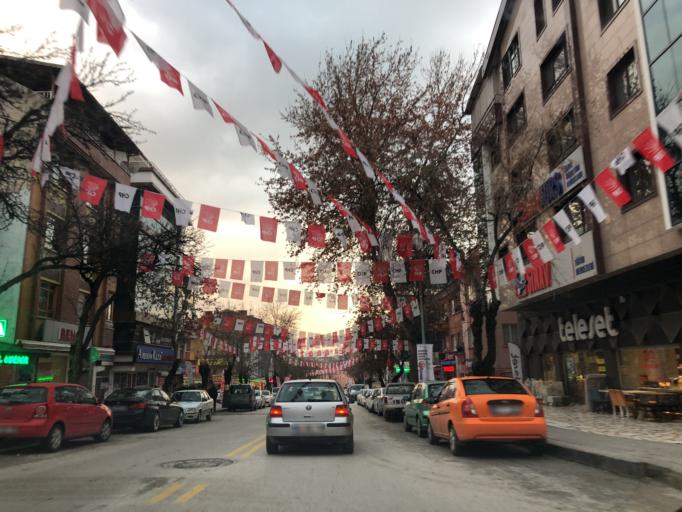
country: TR
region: Ankara
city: Ankara
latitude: 39.9653
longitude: 32.8087
